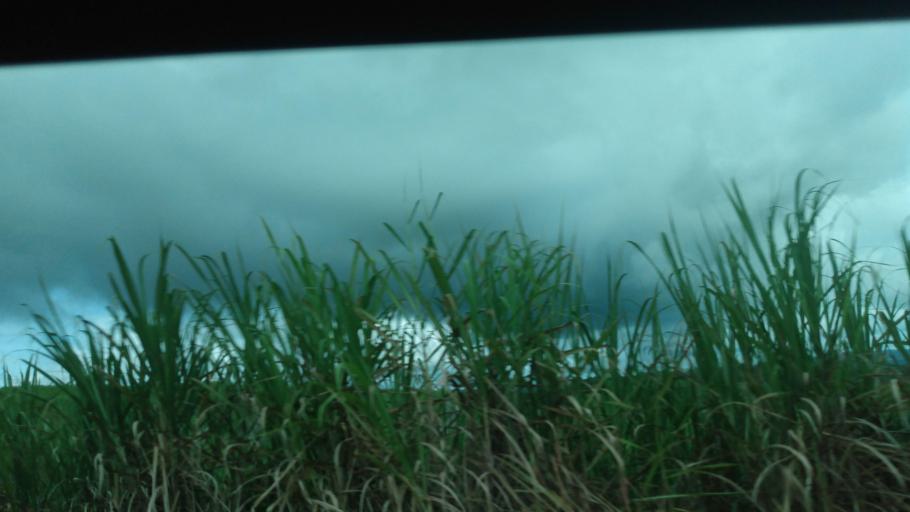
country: BR
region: Pernambuco
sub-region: Quipapa
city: Quipapa
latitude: -8.7991
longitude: -35.9983
